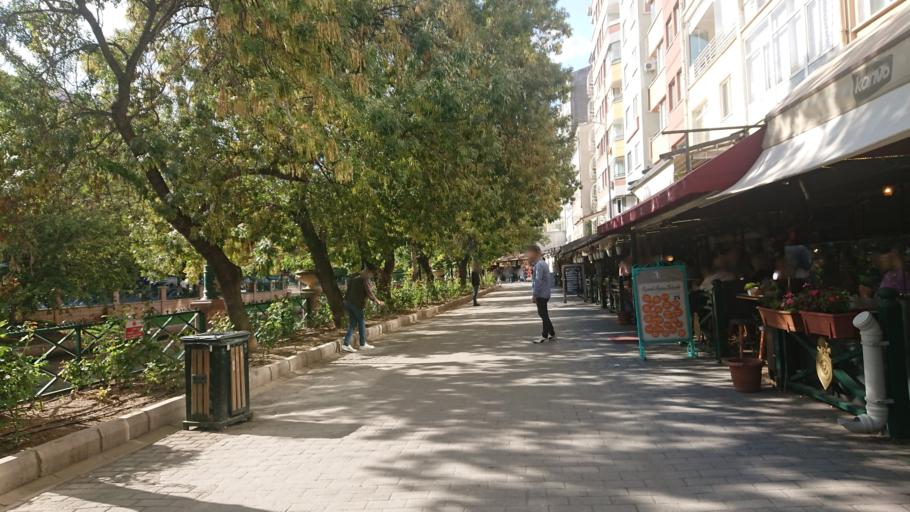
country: TR
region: Eskisehir
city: Eskisehir
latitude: 39.7777
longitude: 30.5157
